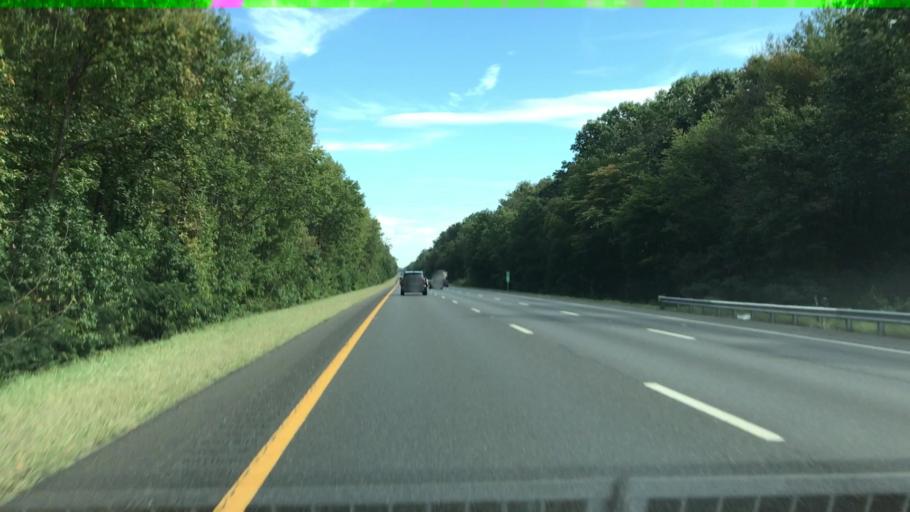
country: US
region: New Jersey
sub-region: Burlington County
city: Roebling
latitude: 40.0702
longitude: -74.7855
